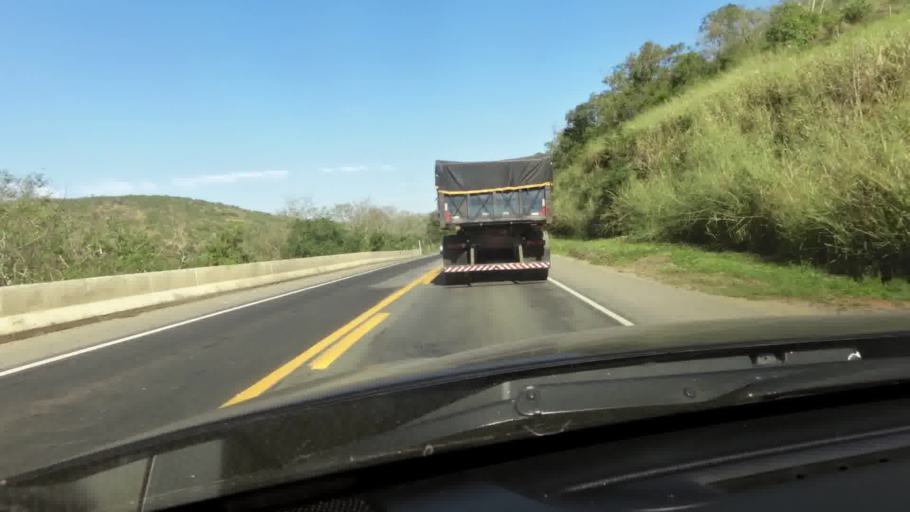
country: BR
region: Espirito Santo
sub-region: Cachoeiro De Itapemirim
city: Cachoeiro de Itapemirim
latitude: -20.9123
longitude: -41.0694
